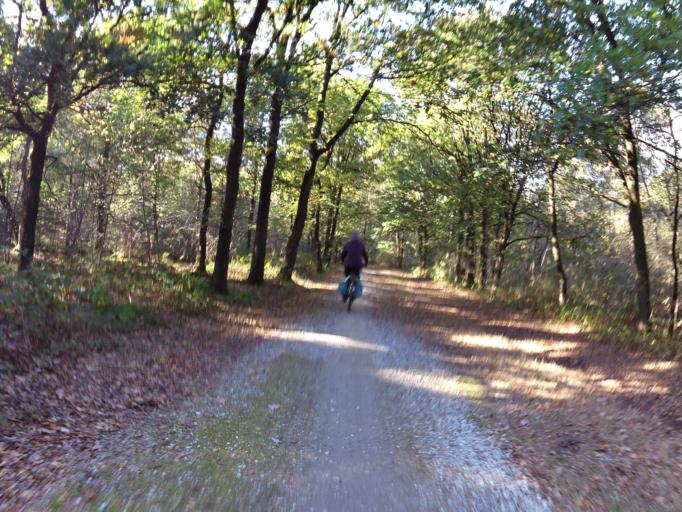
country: NL
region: Limburg
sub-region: Gemeente Bergen
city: Wellerlooi
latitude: 51.5263
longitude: 6.1496
